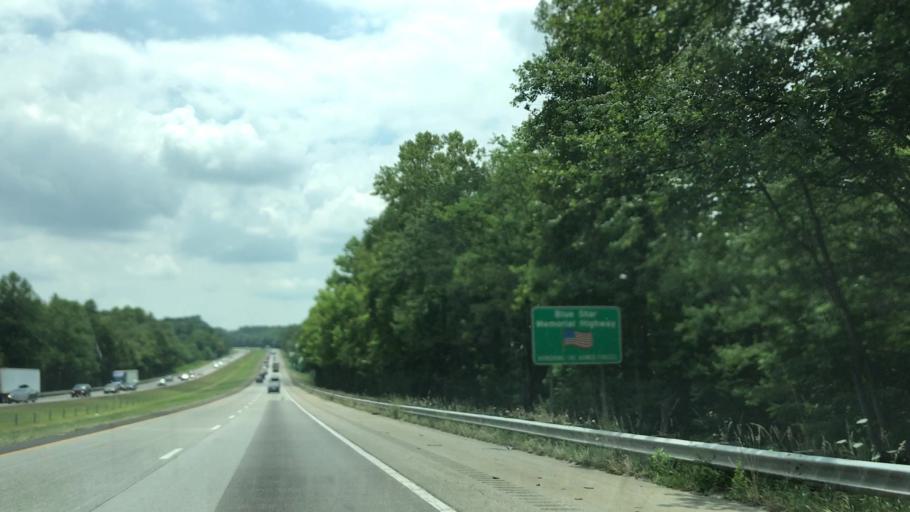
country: US
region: Virginia
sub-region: Carroll County
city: Cana
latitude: 36.5481
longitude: -80.7453
